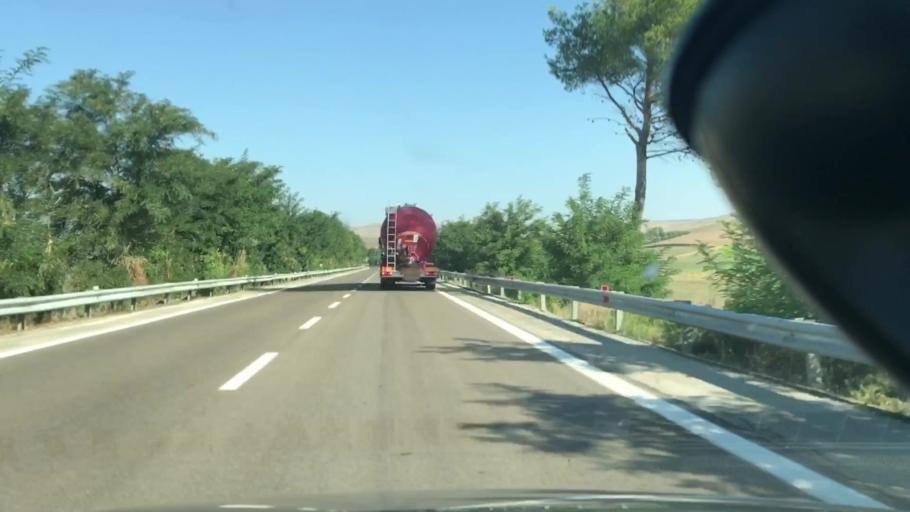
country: IT
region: Basilicate
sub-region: Provincia di Matera
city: Irsina
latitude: 40.8007
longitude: 16.2745
